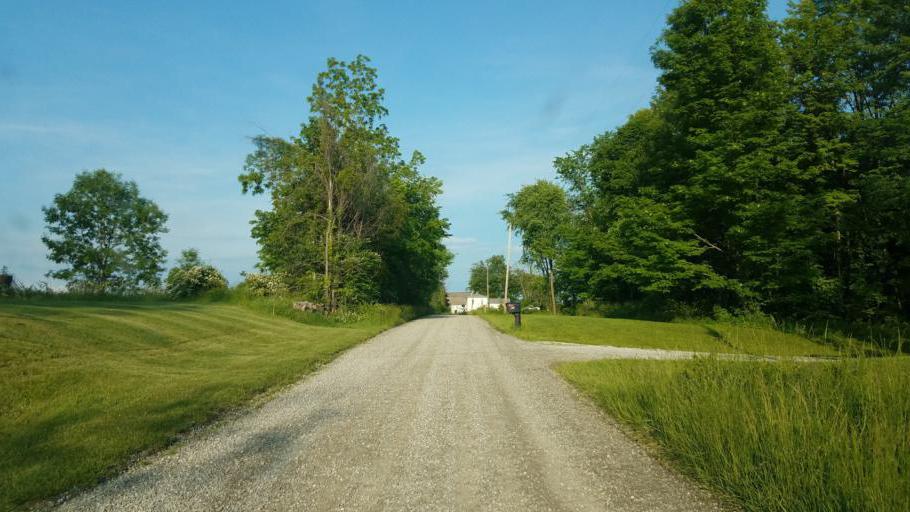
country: US
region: Ohio
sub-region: Morrow County
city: Mount Gilead
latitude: 40.4451
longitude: -82.7395
